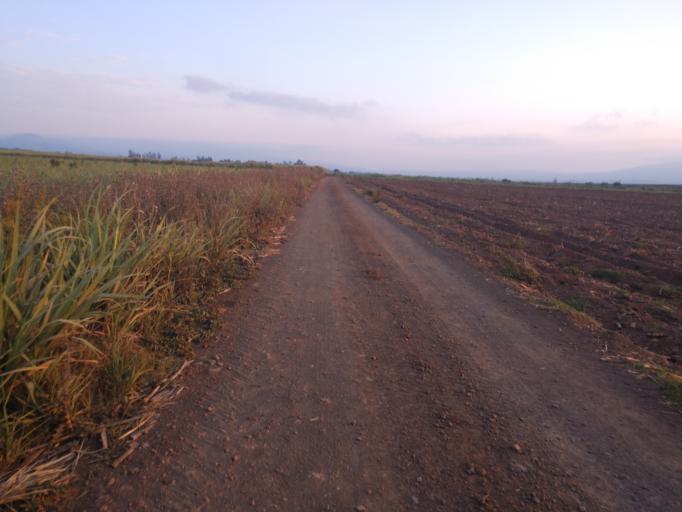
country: MX
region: Nayarit
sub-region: Tepic
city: La Corregidora
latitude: 21.4763
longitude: -104.8069
